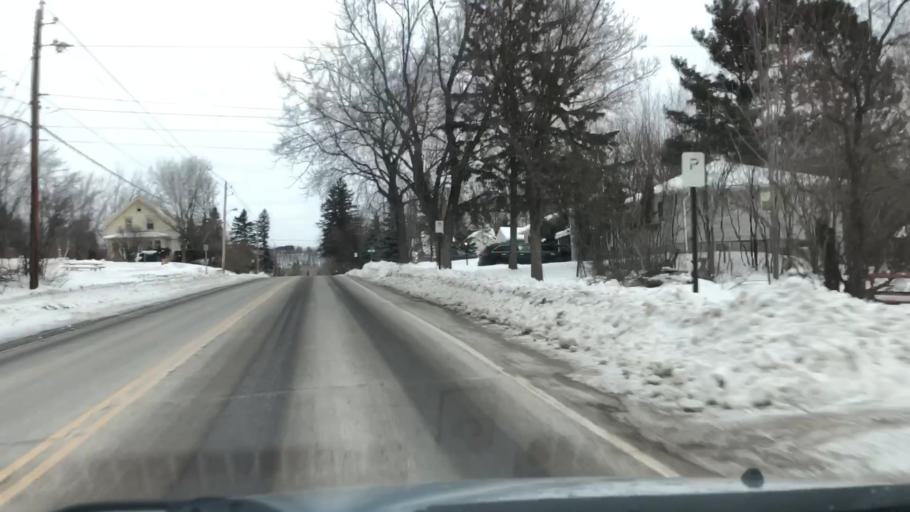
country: US
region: Minnesota
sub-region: Saint Louis County
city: Arnold
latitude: 46.8326
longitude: -92.0368
